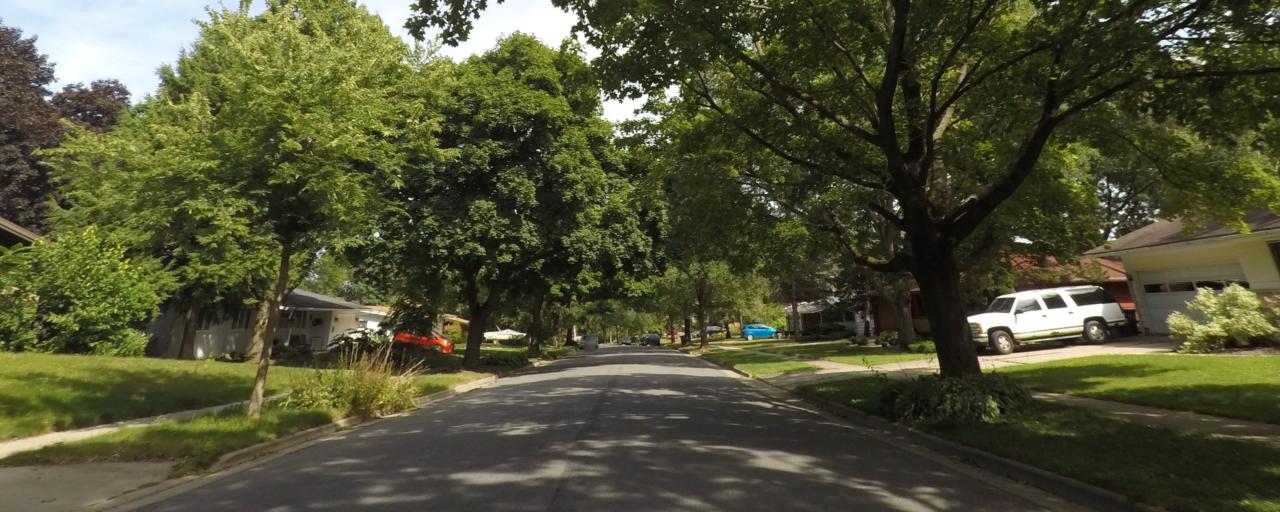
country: US
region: Wisconsin
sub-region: Dane County
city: Shorewood Hills
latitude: 43.0634
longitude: -89.4683
